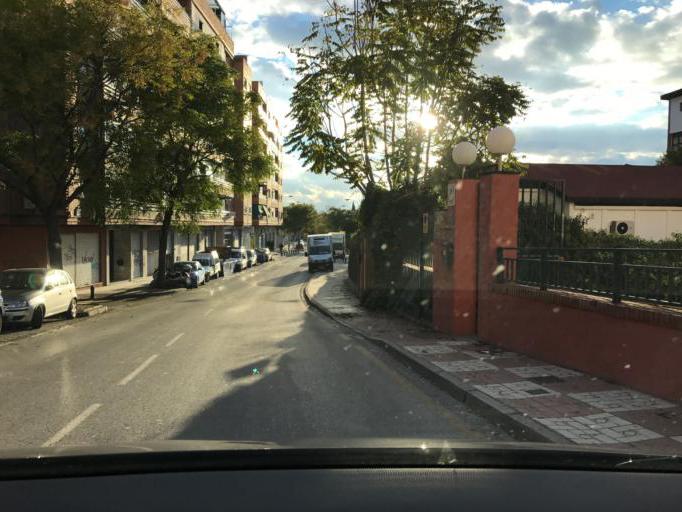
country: ES
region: Andalusia
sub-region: Provincia de Granada
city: Granada
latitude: 37.1833
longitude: -3.6150
